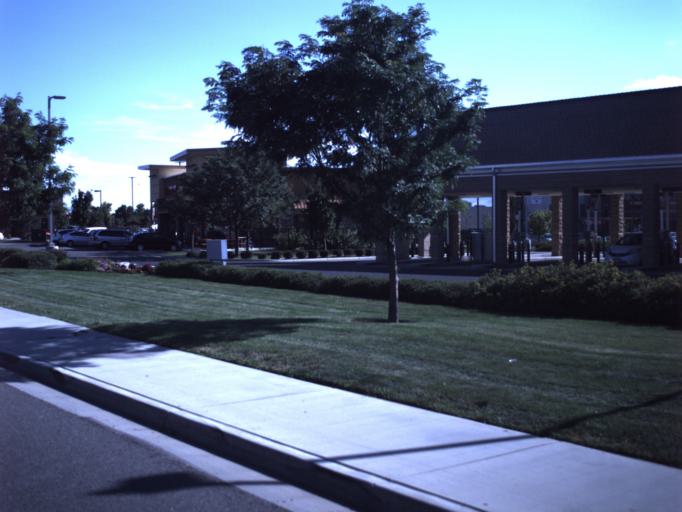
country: US
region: Utah
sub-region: Utah County
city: American Fork
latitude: 40.3825
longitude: -111.8144
